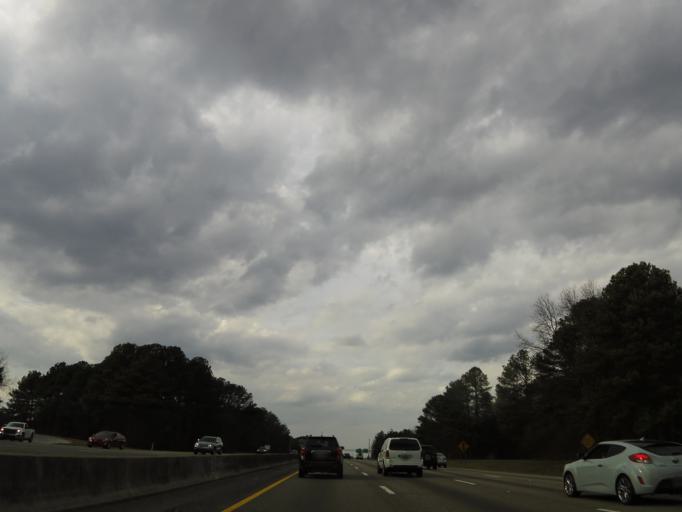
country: US
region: South Carolina
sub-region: Lexington County
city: Saint Andrews
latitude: 34.0343
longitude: -81.1080
